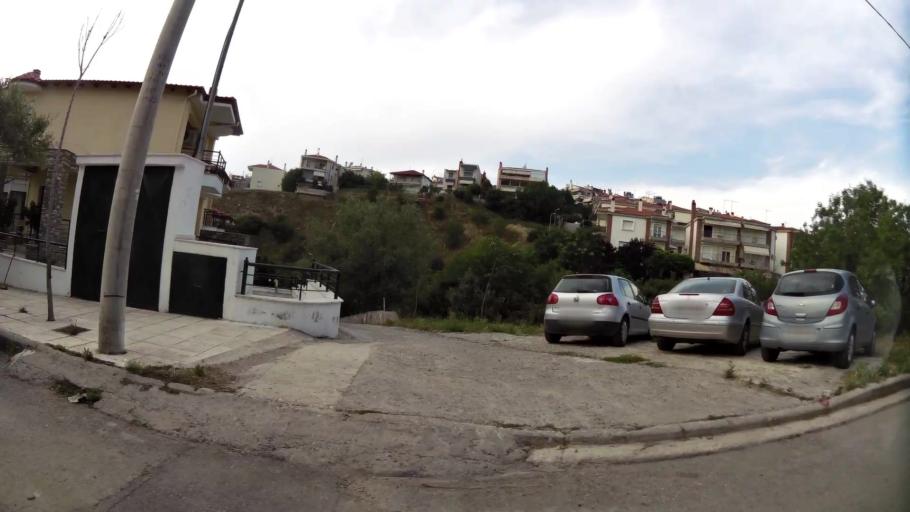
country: GR
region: Central Macedonia
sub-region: Nomos Thessalonikis
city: Pefka
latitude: 40.6610
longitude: 22.9847
